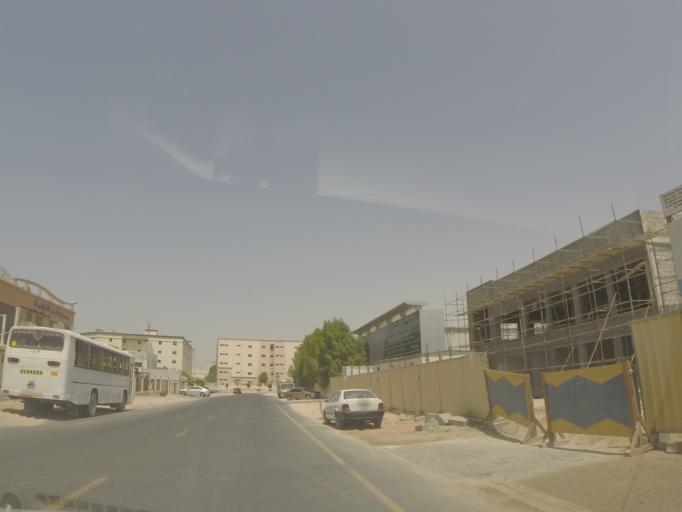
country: AE
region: Dubai
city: Dubai
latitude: 24.9831
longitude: 55.1972
